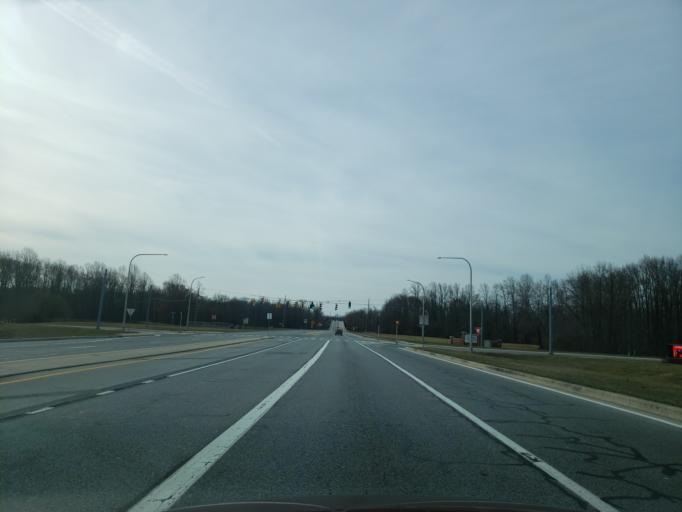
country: US
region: Delaware
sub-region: Kent County
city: Cheswold
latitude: 39.1967
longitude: -75.5582
